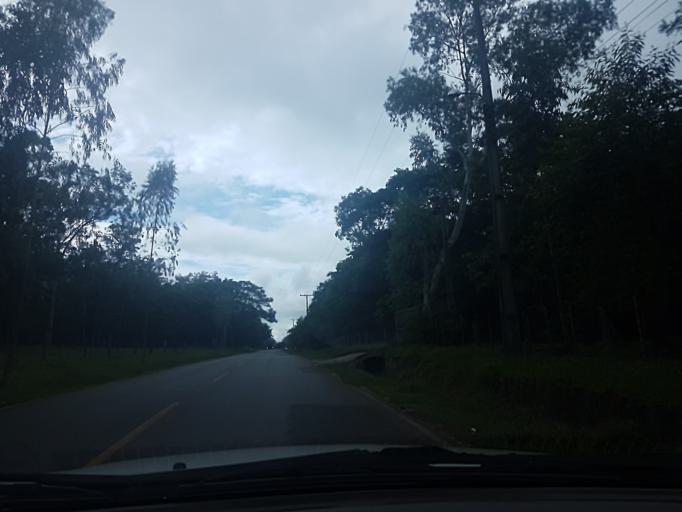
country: PY
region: Central
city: Limpio
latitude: -25.1996
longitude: -57.4535
